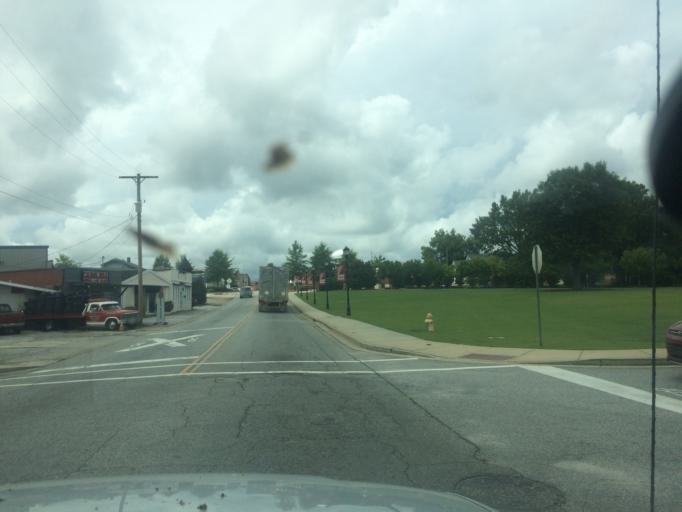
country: US
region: South Carolina
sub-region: Greenville County
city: Greer
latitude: 34.9371
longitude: -82.2239
